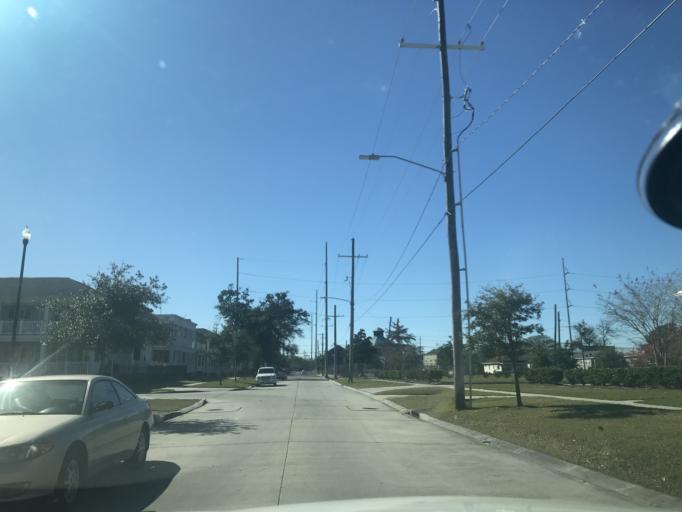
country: US
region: Louisiana
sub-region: Orleans Parish
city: New Orleans
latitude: 29.9537
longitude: -90.0951
